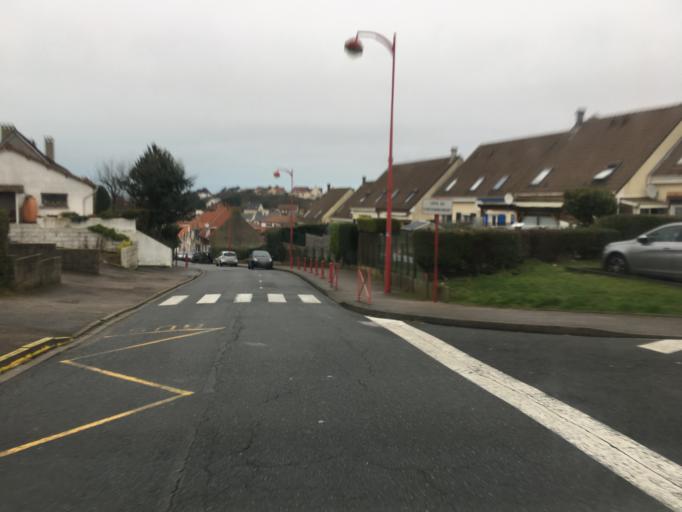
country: FR
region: Nord-Pas-de-Calais
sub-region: Departement du Pas-de-Calais
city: Equihen-Plage
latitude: 50.6778
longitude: 1.5749
